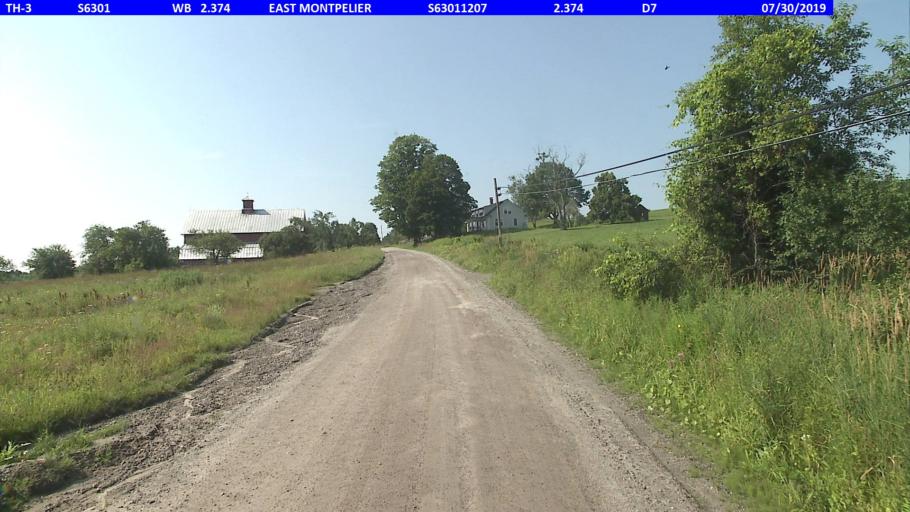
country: US
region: Vermont
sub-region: Washington County
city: Montpelier
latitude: 44.2926
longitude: -72.5194
